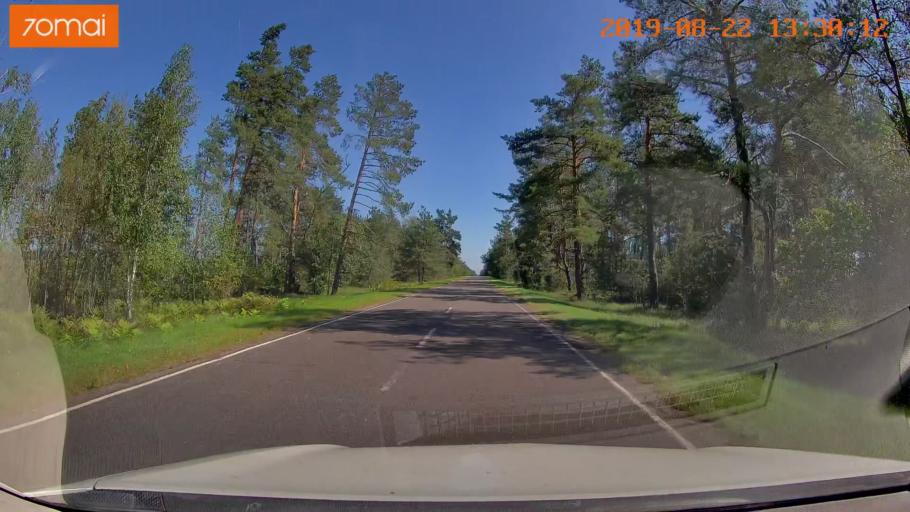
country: BY
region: Minsk
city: Staryya Darohi
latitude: 53.2173
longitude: 28.1504
